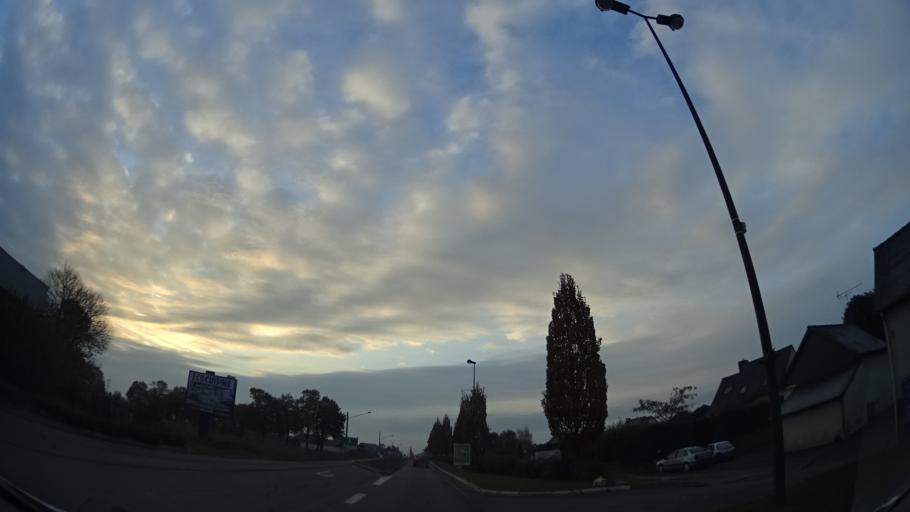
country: FR
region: Brittany
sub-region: Departement d'Ille-et-Vilaine
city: La Chapelle-des-Fougeretz
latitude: 48.1987
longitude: -1.7335
